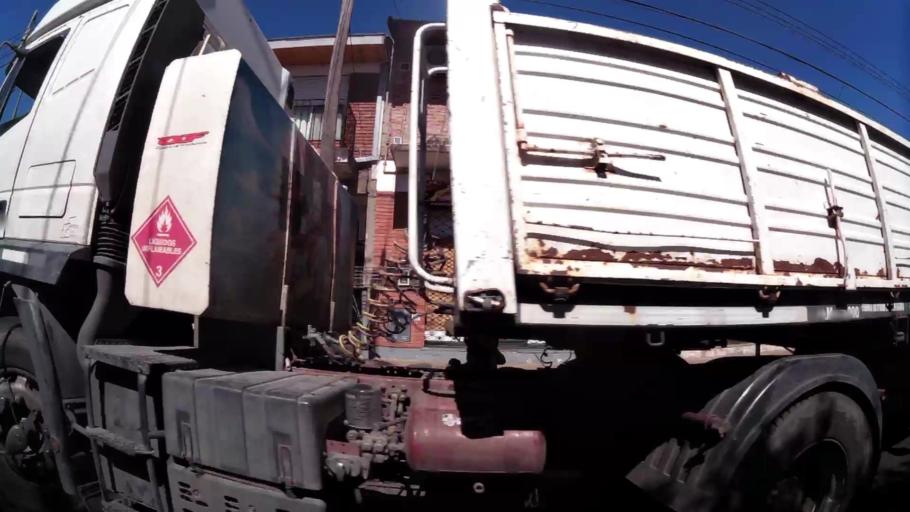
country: AR
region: Buenos Aires
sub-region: Partido de Tigre
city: Tigre
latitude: -34.4888
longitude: -58.6137
